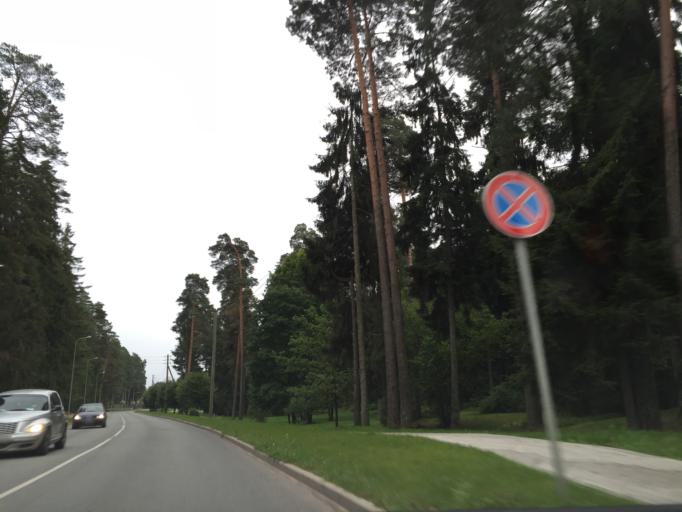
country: LV
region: Ogre
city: Ogre
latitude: 56.8188
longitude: 24.6153
